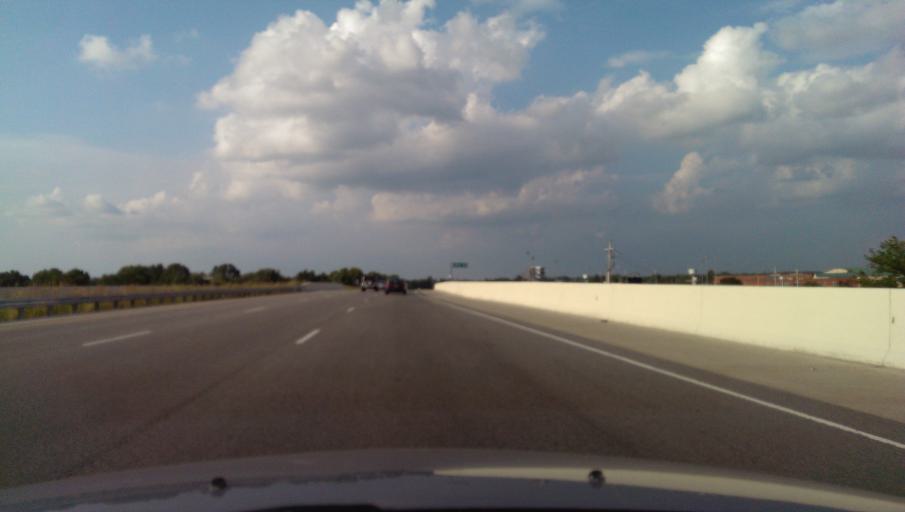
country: US
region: Indiana
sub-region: Hamilton County
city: Westfield
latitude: 40.0491
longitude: -86.1347
